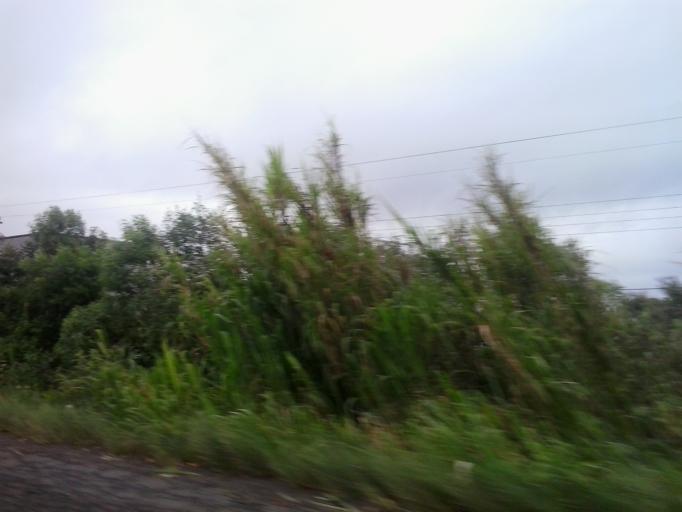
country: BR
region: Rio Grande do Sul
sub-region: Santa Maria
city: Santa Maria
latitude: -29.7226
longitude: -53.3878
